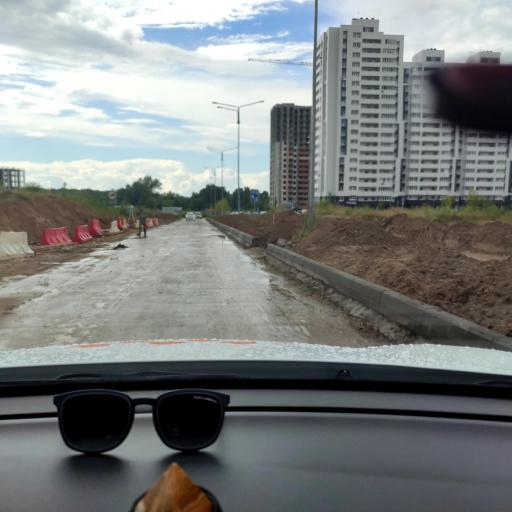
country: RU
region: Tatarstan
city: Osinovo
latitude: 55.8444
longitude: 48.9099
